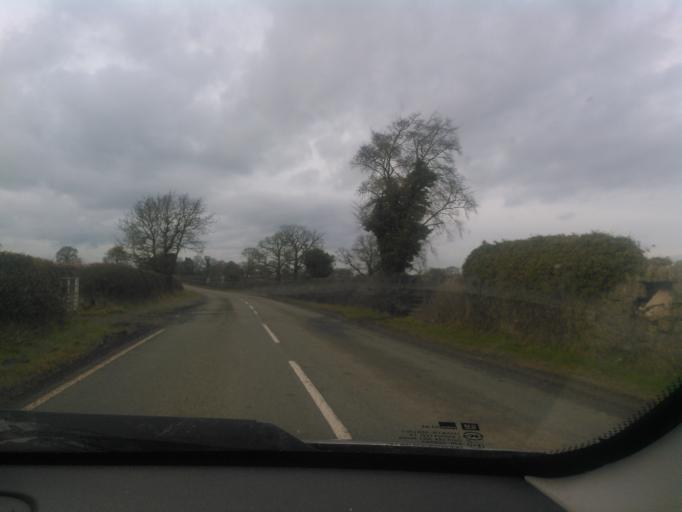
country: GB
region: England
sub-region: Shropshire
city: Wem
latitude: 52.8345
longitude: -2.6997
